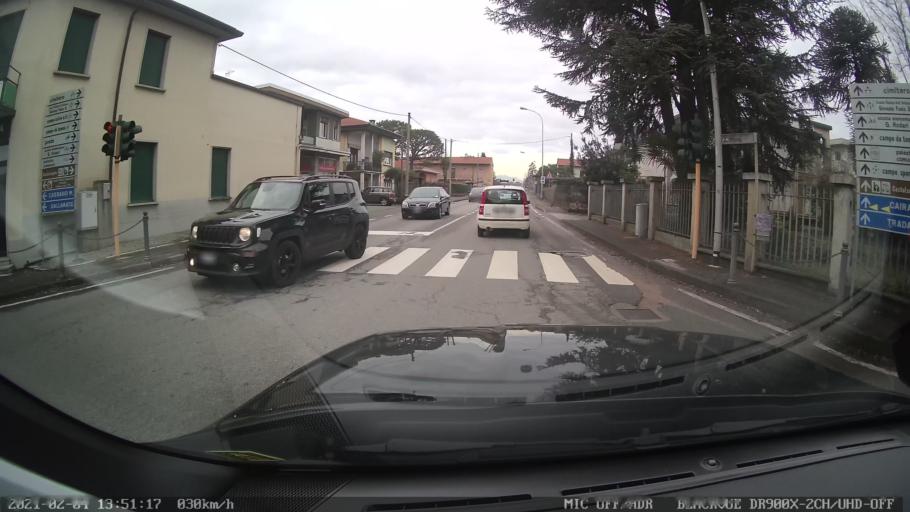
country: IT
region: Lombardy
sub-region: Provincia di Varese
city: Fagnano Olona-Bergoro
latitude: 45.6685
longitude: 8.8668
